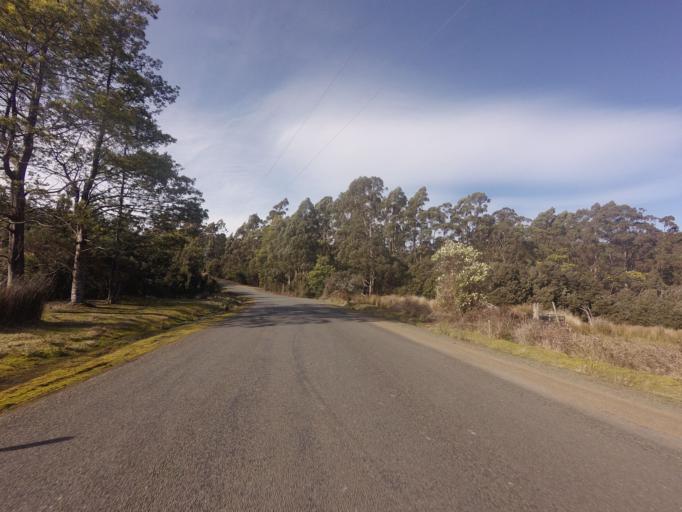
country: AU
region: Tasmania
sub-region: Kingborough
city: Kettering
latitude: -43.1704
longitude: 147.1961
